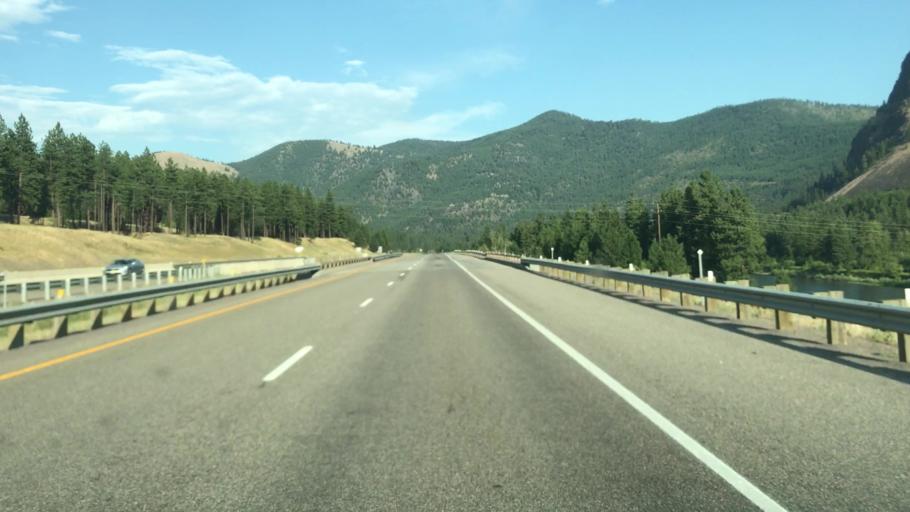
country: US
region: Montana
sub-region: Missoula County
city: Frenchtown
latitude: 46.9935
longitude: -114.4464
